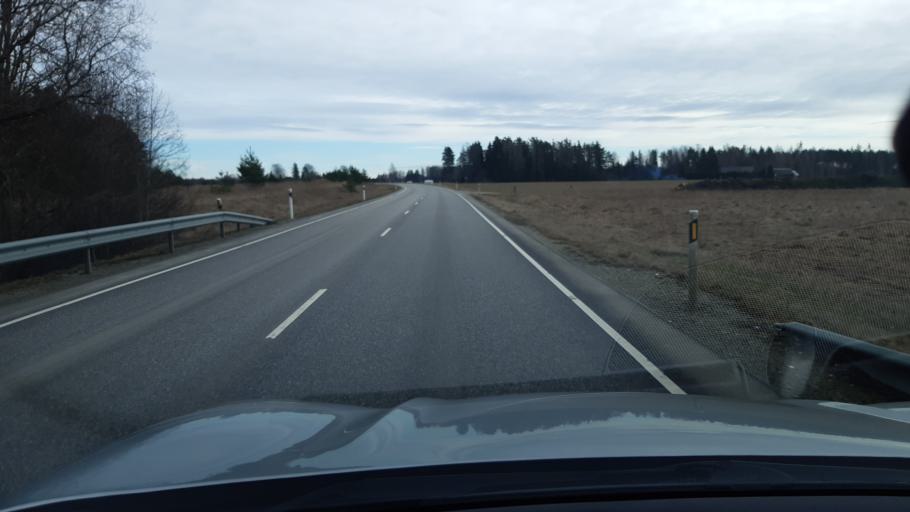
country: EE
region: Raplamaa
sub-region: Kehtna vald
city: Kehtna
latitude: 58.8924
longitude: 24.9098
